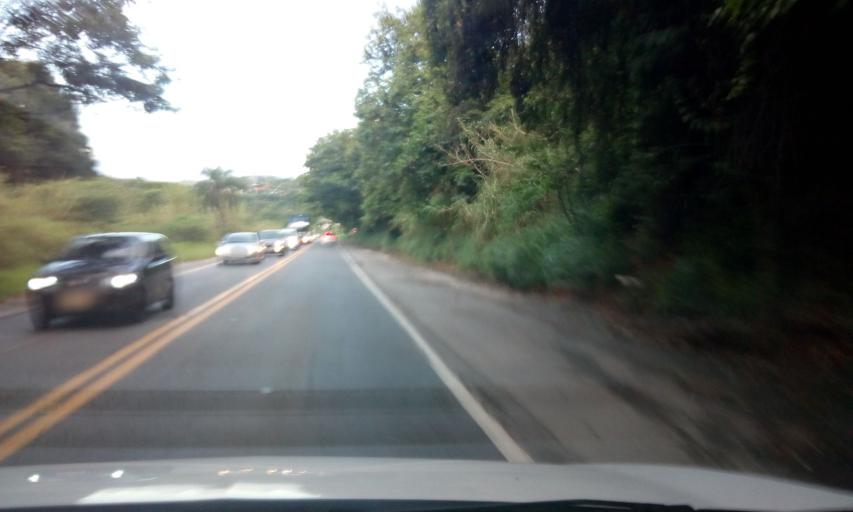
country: BR
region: Sao Paulo
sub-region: Itatiba
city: Itatiba
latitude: -23.0017
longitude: -46.8120
